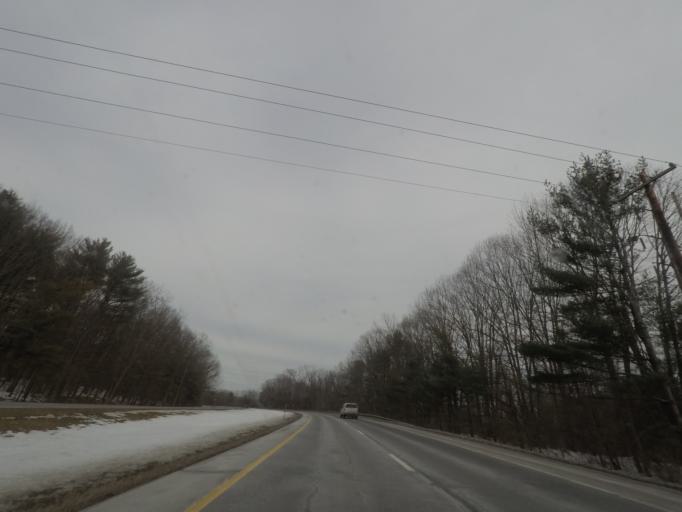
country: US
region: New York
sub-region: Albany County
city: Delmar
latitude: 42.6051
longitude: -73.8267
